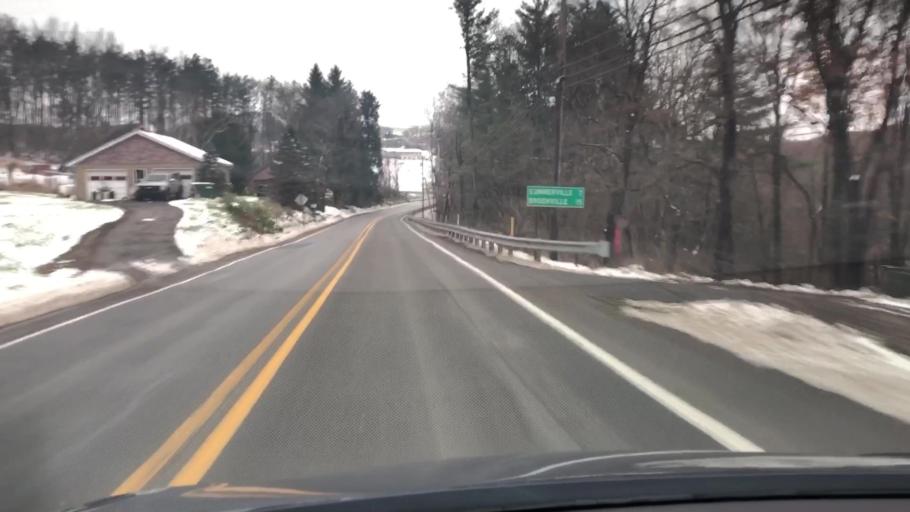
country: US
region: Pennsylvania
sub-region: Clarion County
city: Clarion
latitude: 41.0281
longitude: -79.2649
